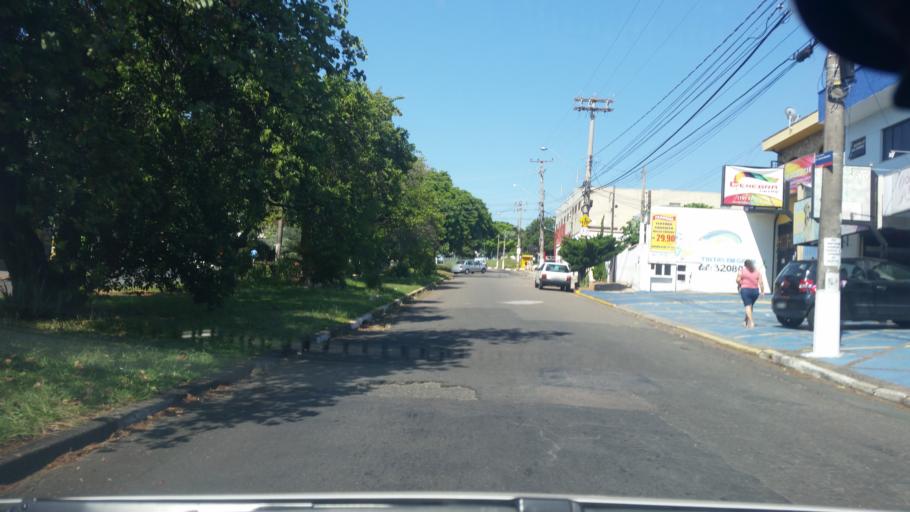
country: BR
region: Sao Paulo
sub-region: Campinas
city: Campinas
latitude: -22.8518
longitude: -47.0680
